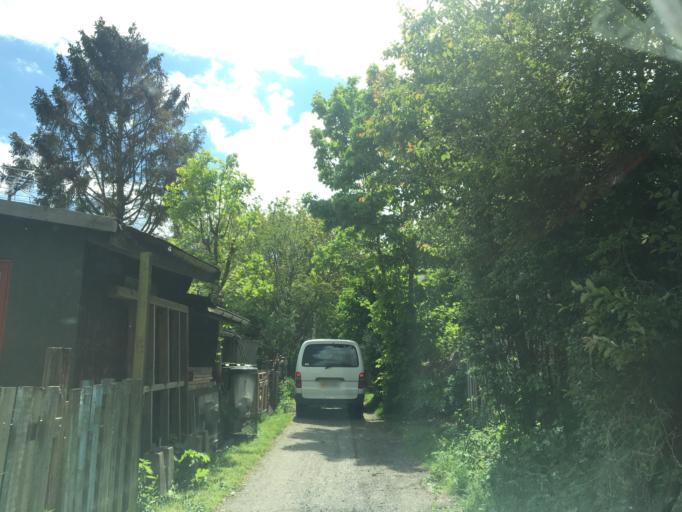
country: DK
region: Capital Region
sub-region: Frederiksberg Kommune
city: Frederiksberg
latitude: 55.6402
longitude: 12.5312
